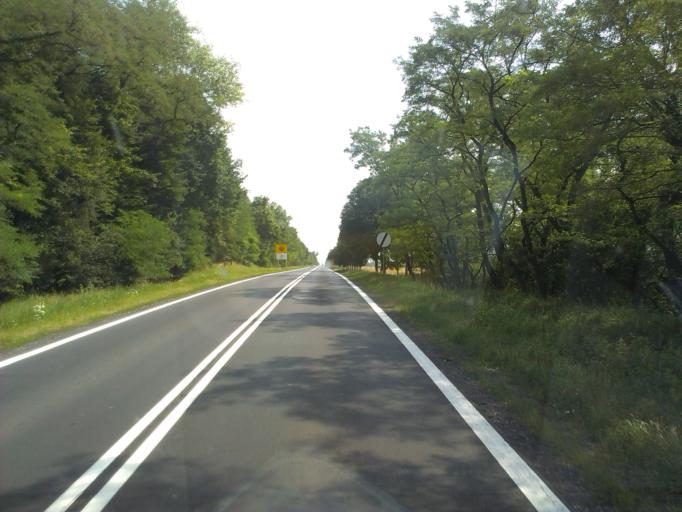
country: PL
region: Lower Silesian Voivodeship
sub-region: Powiat sredzki
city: Malczyce
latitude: 51.2235
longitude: 16.4401
